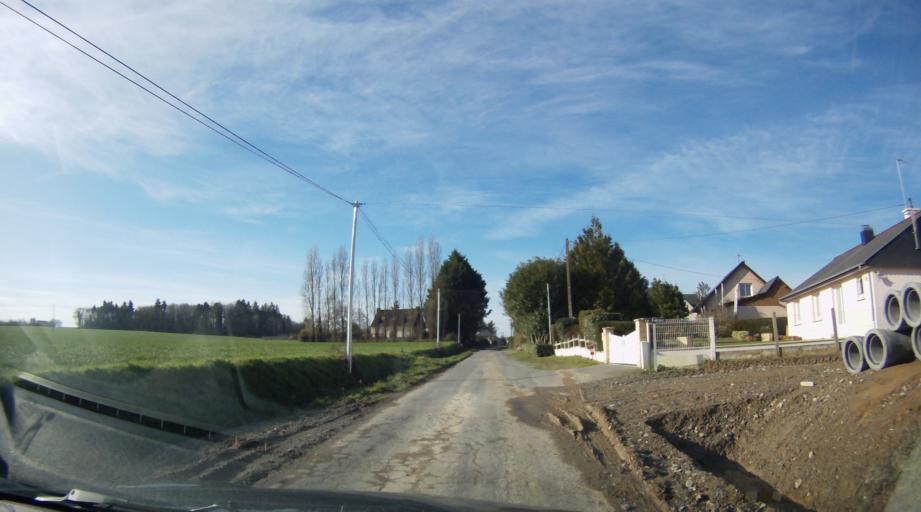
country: FR
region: Brittany
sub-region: Departement d'Ille-et-Vilaine
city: Bourgbarre
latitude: 47.9912
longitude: -1.6208
